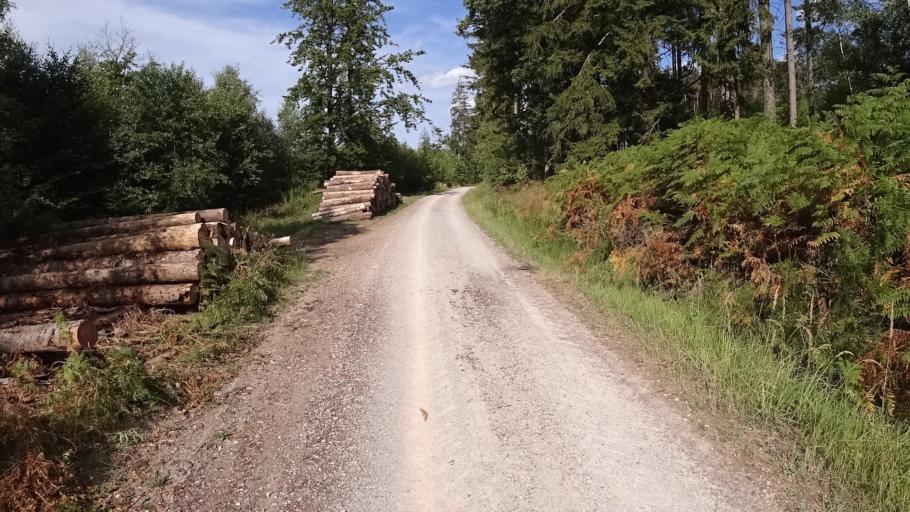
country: DE
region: Rheinland-Pfalz
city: Dichtelbach
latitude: 49.9922
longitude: 7.7116
